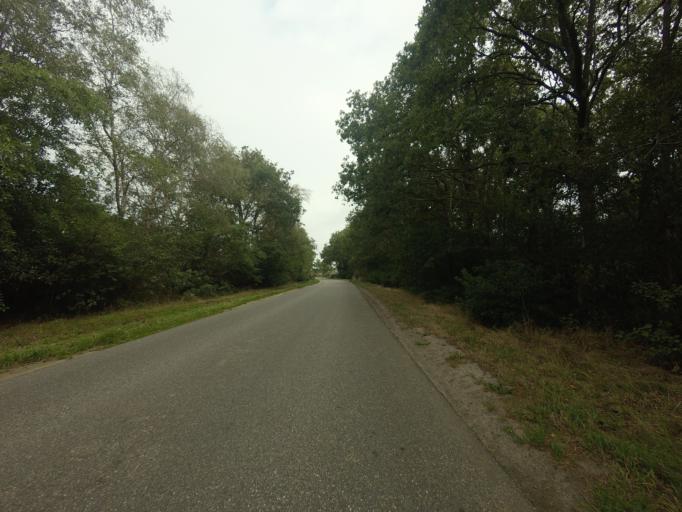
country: NL
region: Friesland
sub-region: Gemeente Heerenveen
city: Jubbega
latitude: 52.9723
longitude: 6.1902
